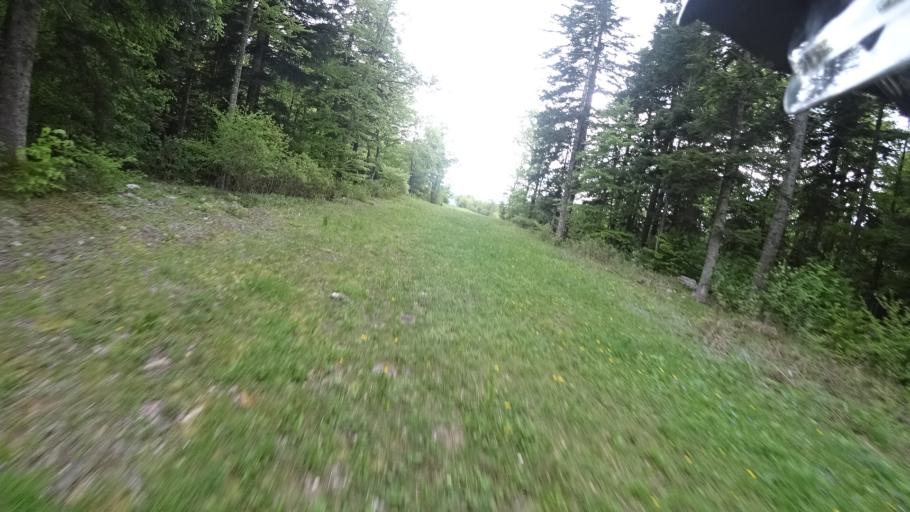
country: HR
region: Karlovacka
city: Plaski
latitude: 44.9095
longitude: 15.4216
